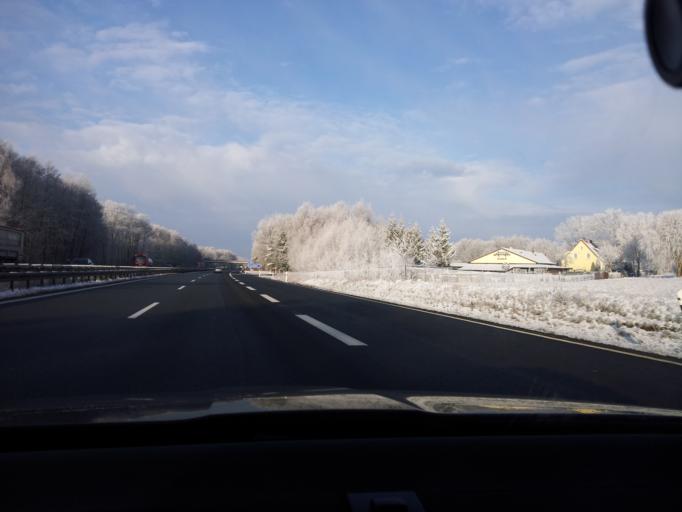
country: DE
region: Brandenburg
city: Putlitz
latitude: 53.2775
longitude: 12.0898
